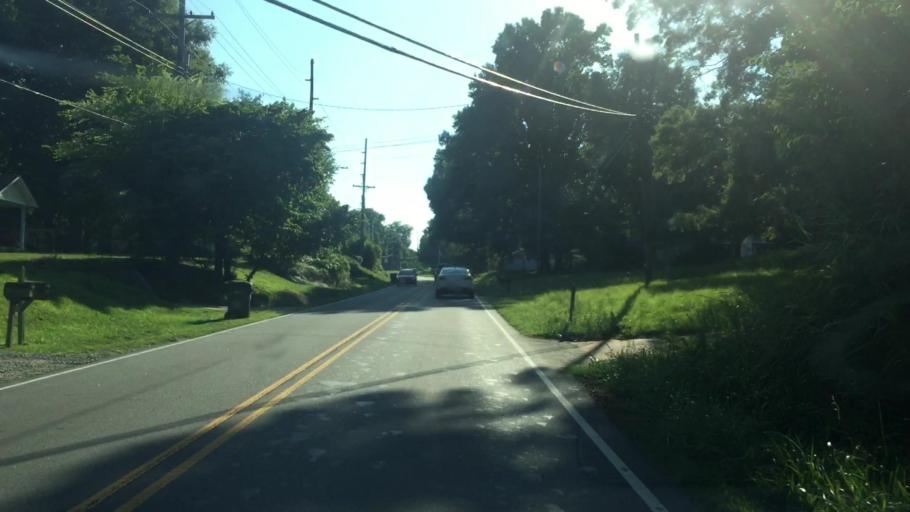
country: US
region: North Carolina
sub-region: Cabarrus County
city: Concord
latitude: 35.4123
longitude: -80.6289
